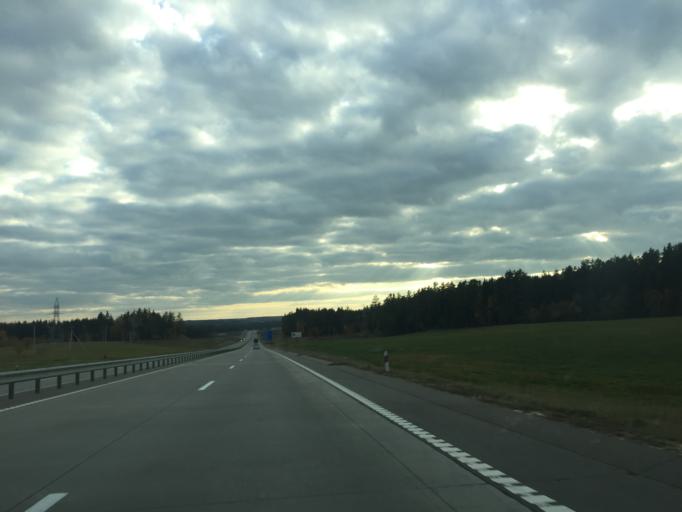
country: BY
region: Minsk
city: Rakaw
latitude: 53.9777
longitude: 27.0972
